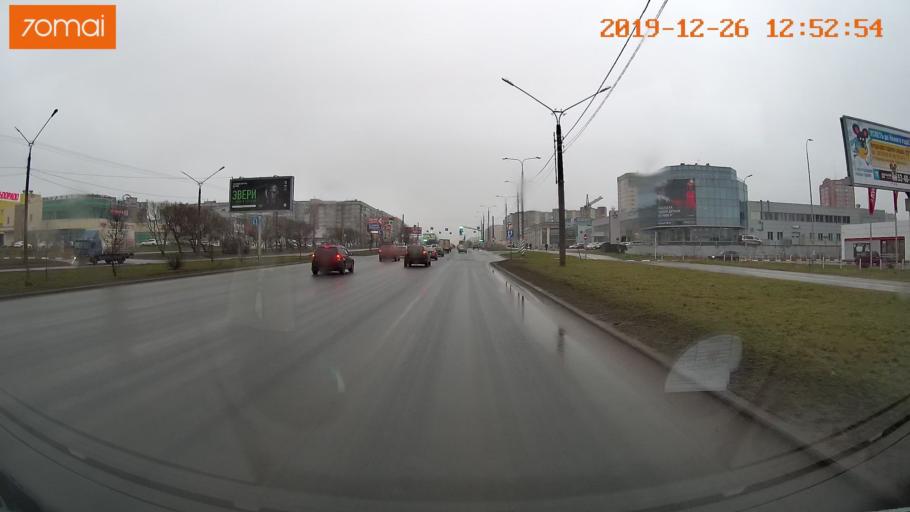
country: RU
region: Vologda
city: Cherepovets
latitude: 59.1001
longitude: 37.9094
